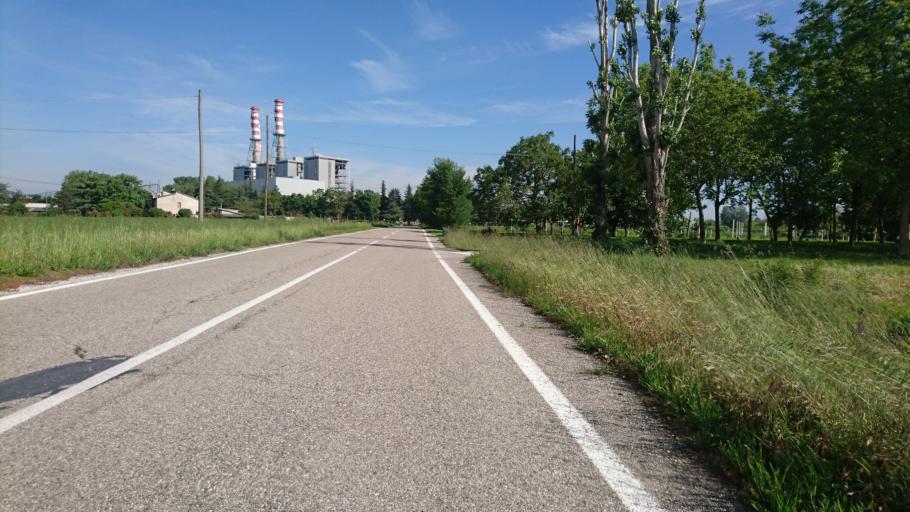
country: IT
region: Lombardy
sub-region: Provincia di Mantova
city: Carbonara di Po
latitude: 45.0212
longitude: 11.2559
